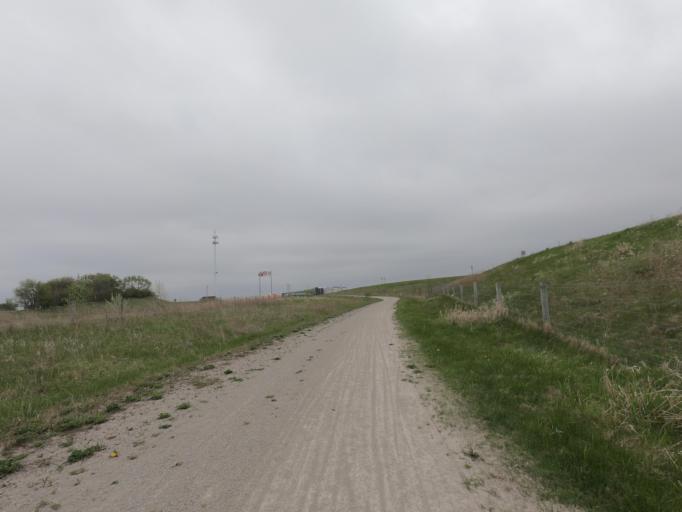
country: US
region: Wisconsin
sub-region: Jefferson County
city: Jefferson
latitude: 43.0342
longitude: -88.8035
